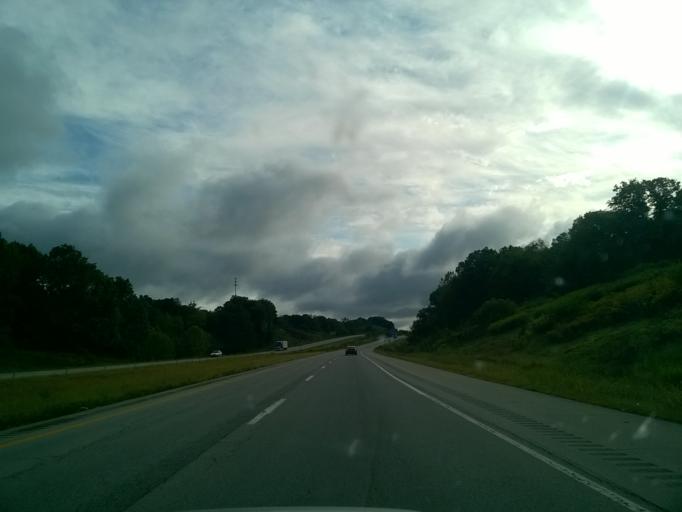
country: US
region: Indiana
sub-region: Crawford County
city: English
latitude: 38.2280
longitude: -86.5814
